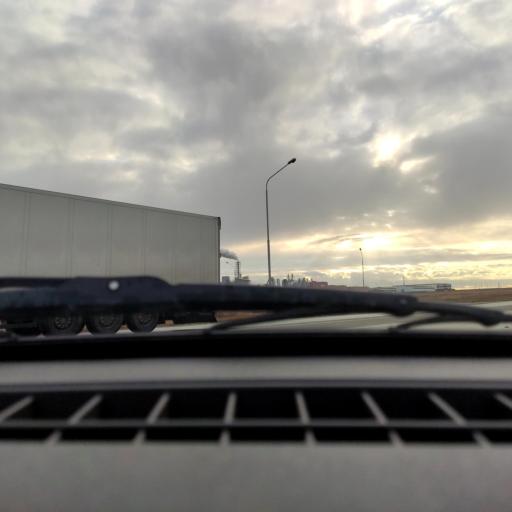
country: RU
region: Bashkortostan
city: Iglino
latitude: 54.7700
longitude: 56.2595
